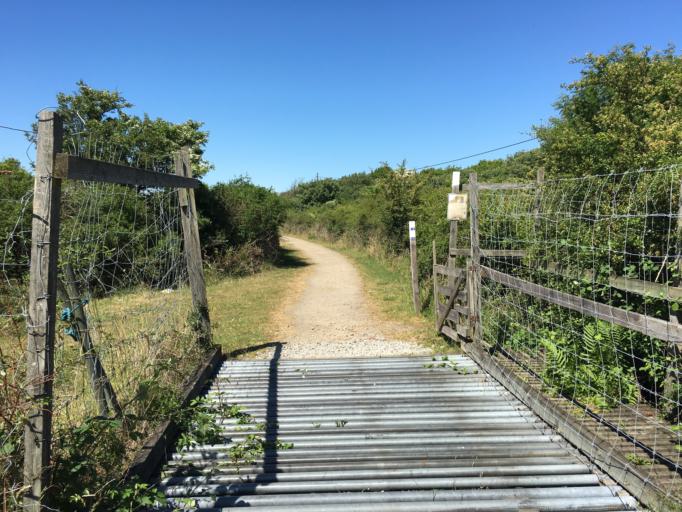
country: SE
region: Blekinge
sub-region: Karlshamns Kommun
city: Karlshamn
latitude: 56.0128
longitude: 14.8356
